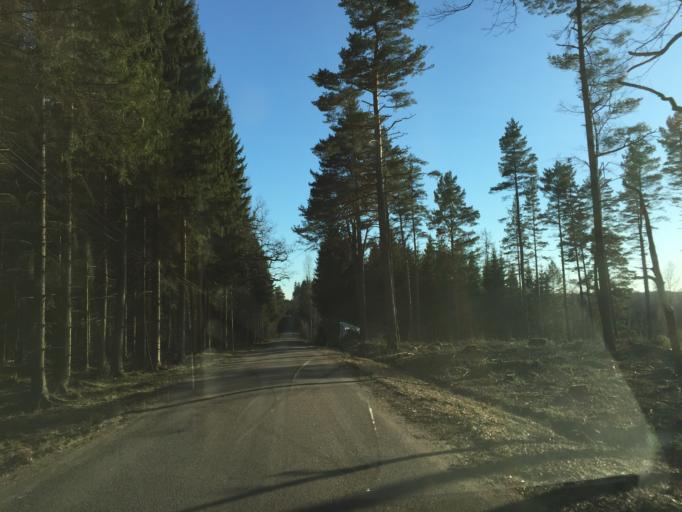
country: SE
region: Soedermanland
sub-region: Vingakers Kommun
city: Vingaker
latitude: 59.0158
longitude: 15.6774
